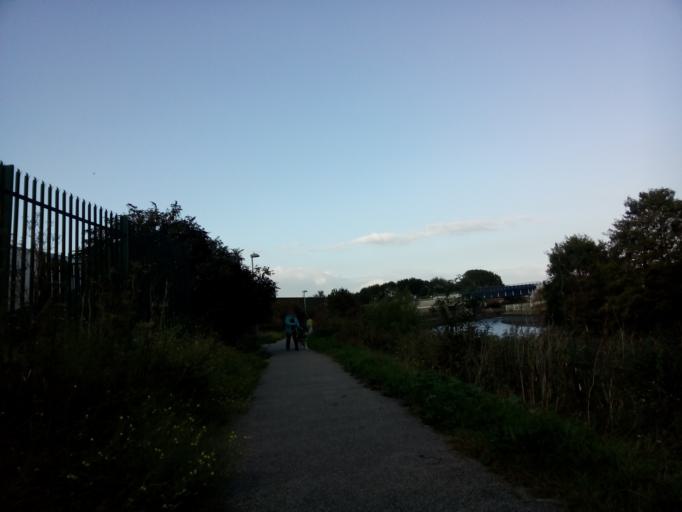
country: GB
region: England
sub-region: Suffolk
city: Bramford
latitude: 52.0631
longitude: 1.1238
